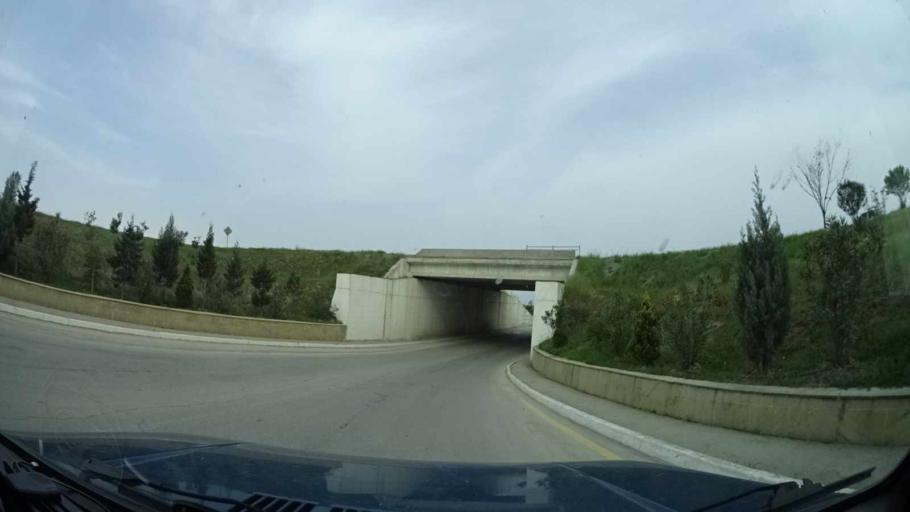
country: AZ
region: Siazan Rayon
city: Kyzyl-Burun
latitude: 41.0686
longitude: 49.1328
